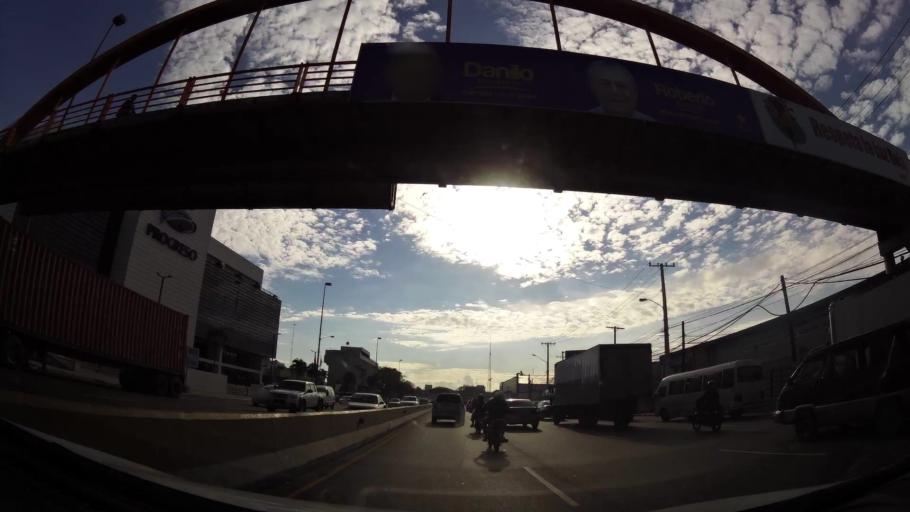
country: DO
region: Nacional
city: San Carlos
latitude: 18.4818
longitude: -69.9111
